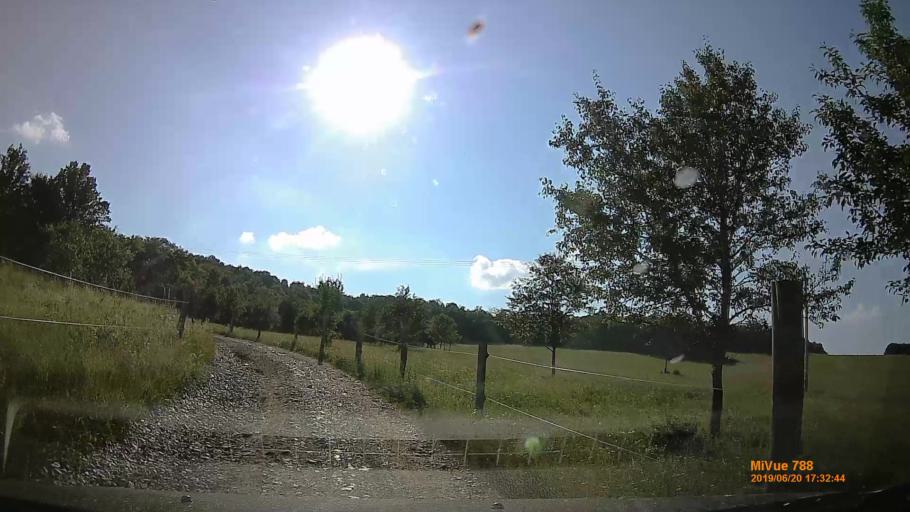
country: HU
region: Baranya
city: Buekkoesd
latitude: 46.1498
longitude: 18.0084
